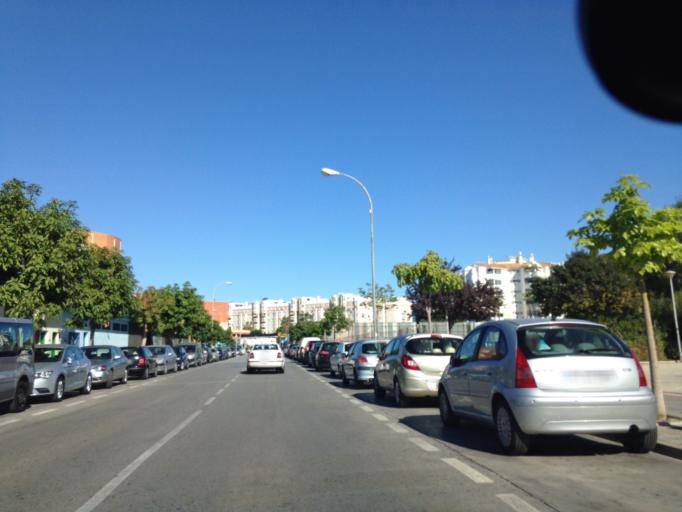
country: ES
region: Andalusia
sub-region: Provincia de Malaga
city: Malaga
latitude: 36.6892
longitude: -4.4572
